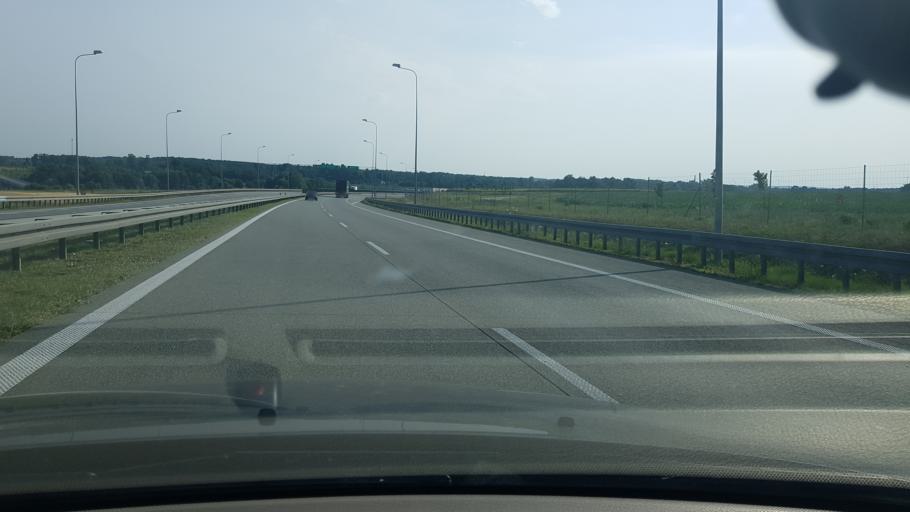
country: PL
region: Lodz Voivodeship
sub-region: Powiat skierniewicki
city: Kowiesy
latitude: 51.8463
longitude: 20.3645
